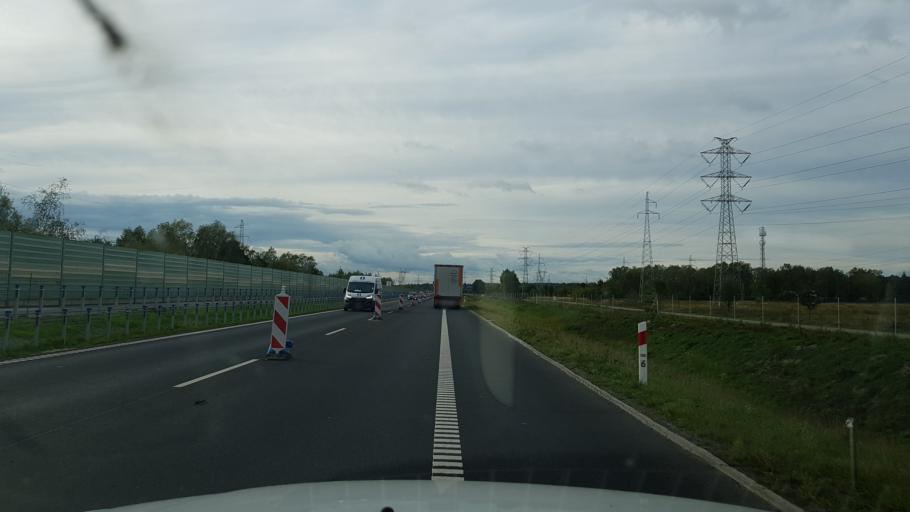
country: PL
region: West Pomeranian Voivodeship
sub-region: Powiat stargardzki
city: Kobylanka
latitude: 53.3584
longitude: 14.9226
